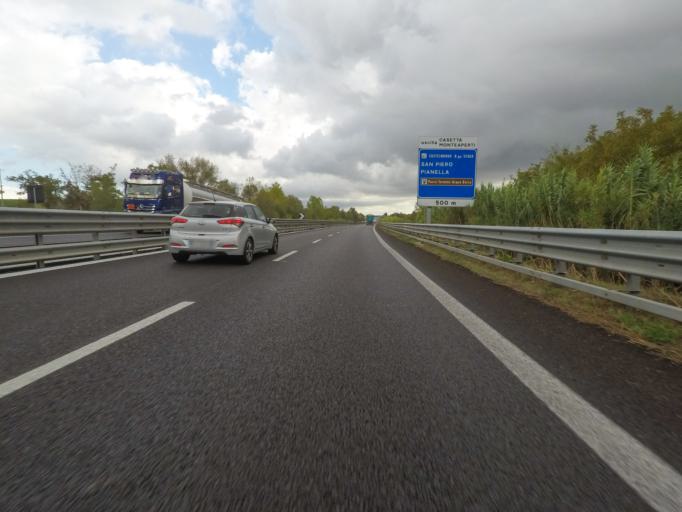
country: IT
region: Tuscany
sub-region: Provincia di Siena
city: Arbia
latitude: 43.3048
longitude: 11.4193
